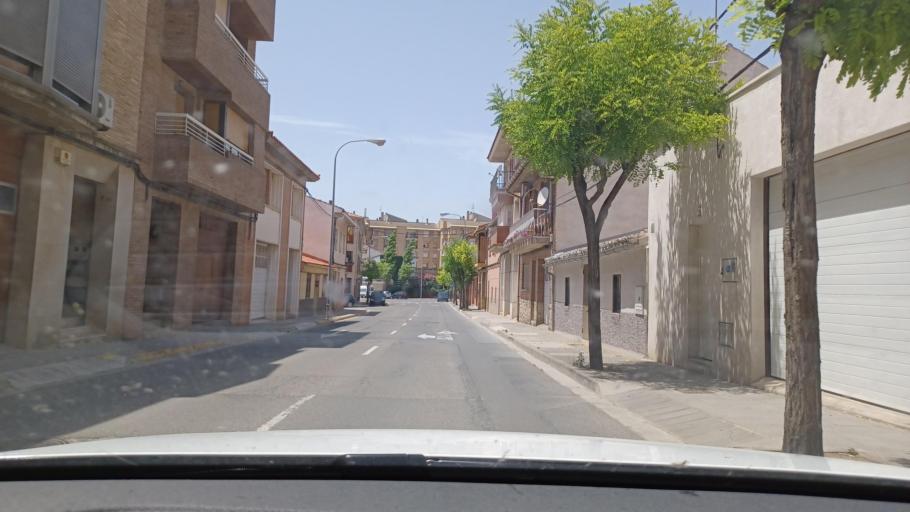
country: ES
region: Navarre
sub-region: Provincia de Navarra
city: Tudela
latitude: 42.0663
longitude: -1.6096
